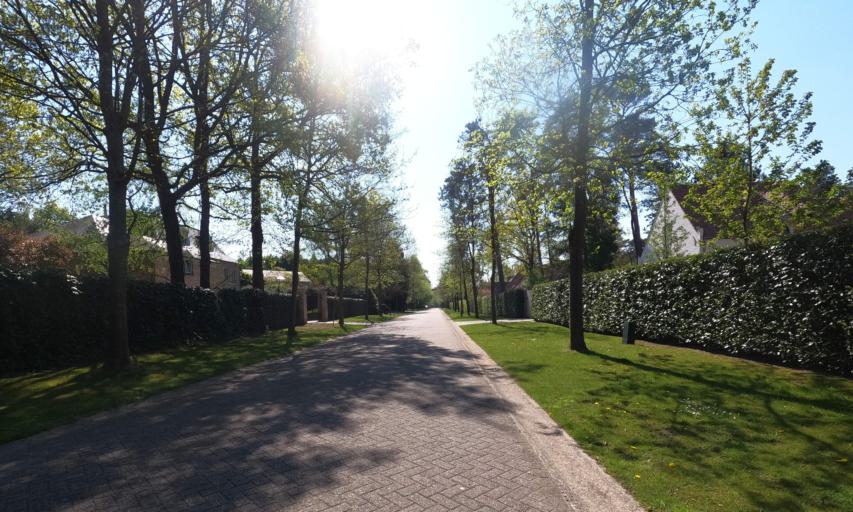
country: BE
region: Flanders
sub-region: Provincie Antwerpen
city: Schilde
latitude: 51.2423
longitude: 4.6132
